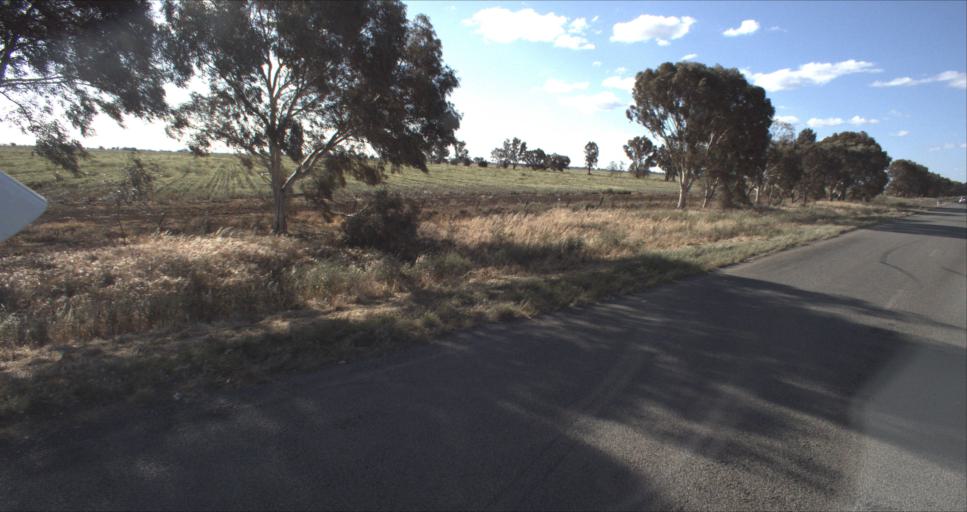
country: AU
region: New South Wales
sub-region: Leeton
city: Leeton
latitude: -34.5504
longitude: 146.2791
